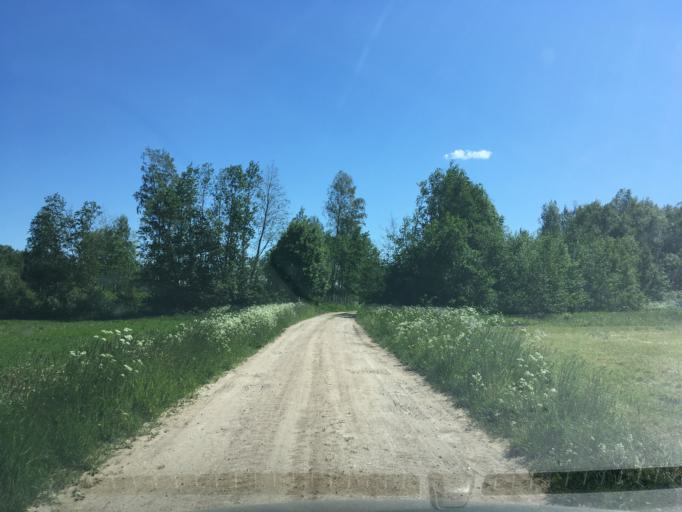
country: EE
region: Harju
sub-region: Raasiku vald
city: Raasiku
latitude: 59.1575
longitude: 25.1346
